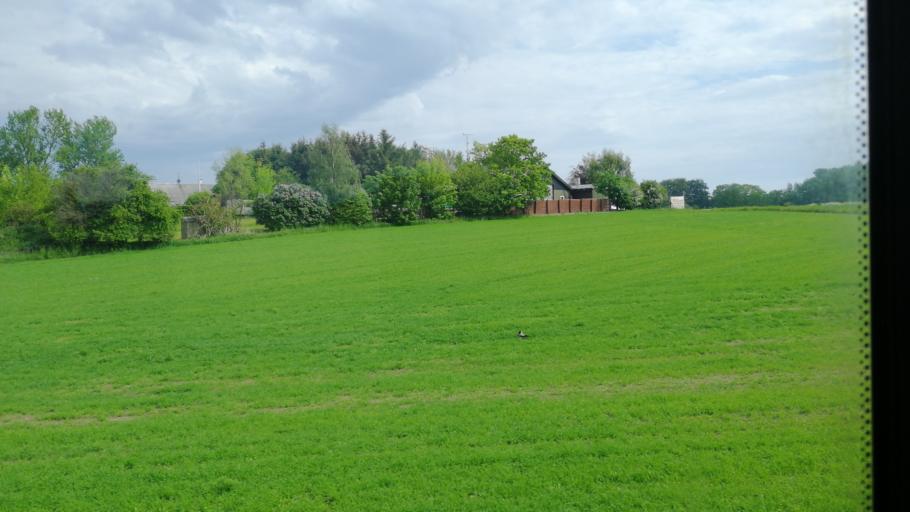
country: DK
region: Capital Region
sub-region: Gribskov Kommune
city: Gilleleje
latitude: 56.1010
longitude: 12.3328
